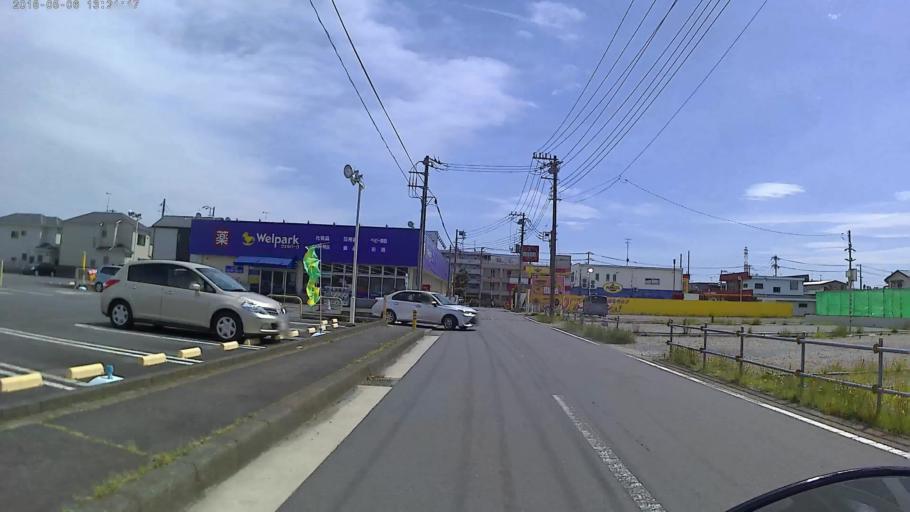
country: JP
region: Kanagawa
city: Fujisawa
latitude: 35.4082
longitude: 139.4479
